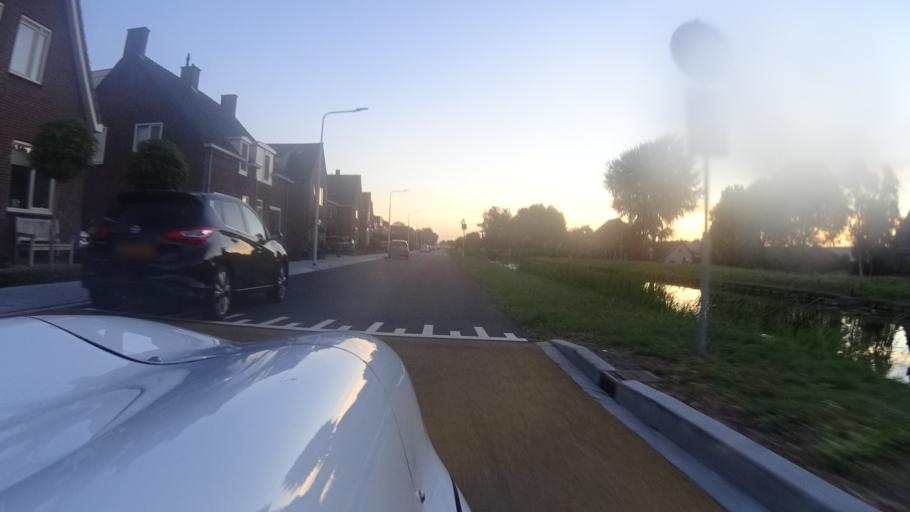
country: NL
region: South Holland
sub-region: Gemeente Kaag en Braassem
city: Oude Wetering
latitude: 52.2021
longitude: 4.6258
